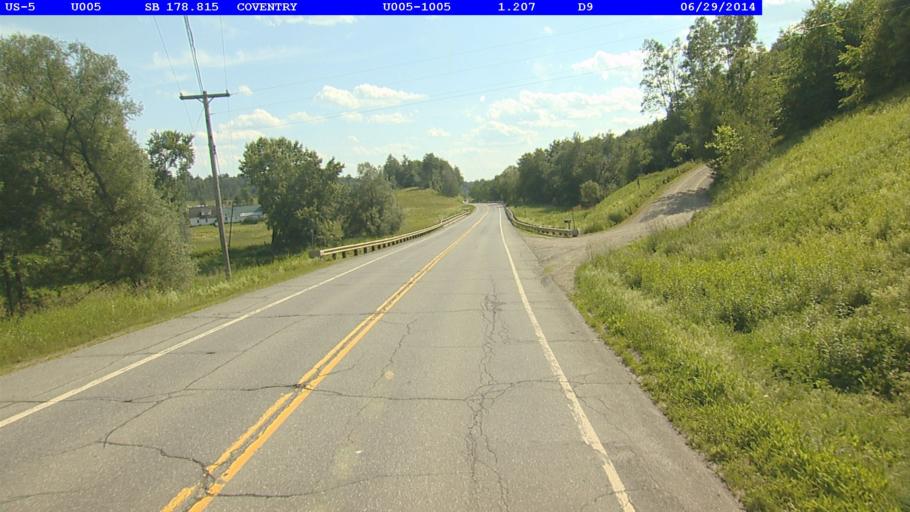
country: US
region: Vermont
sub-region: Orleans County
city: Newport
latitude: 44.8737
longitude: -72.2547
